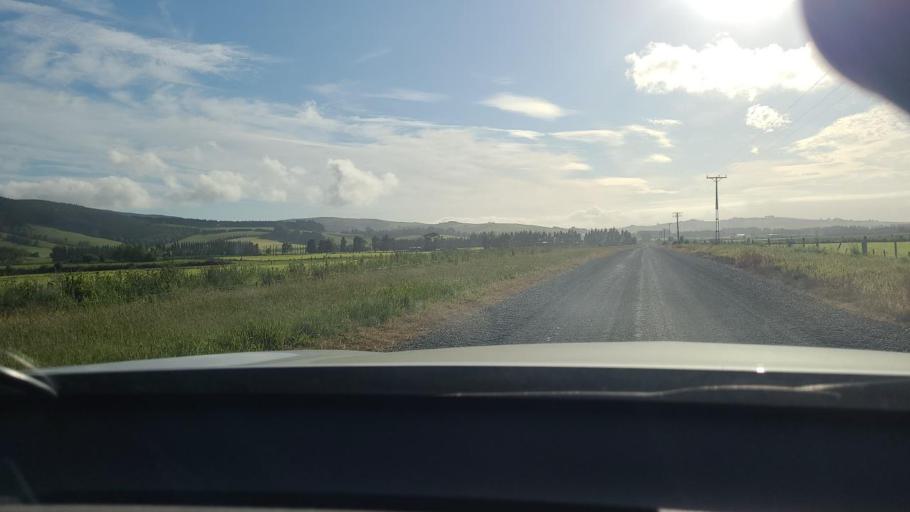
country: NZ
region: Southland
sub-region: Southland District
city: Winton
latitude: -46.0069
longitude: 168.2203
